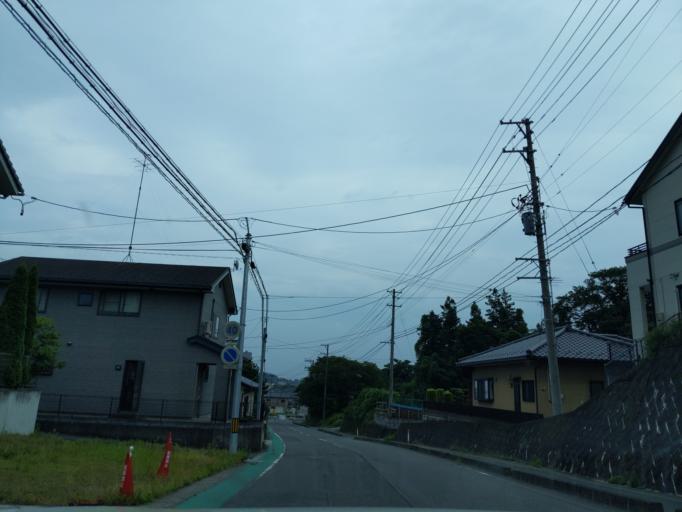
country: JP
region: Fukushima
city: Sukagawa
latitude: 37.3104
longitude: 140.3726
